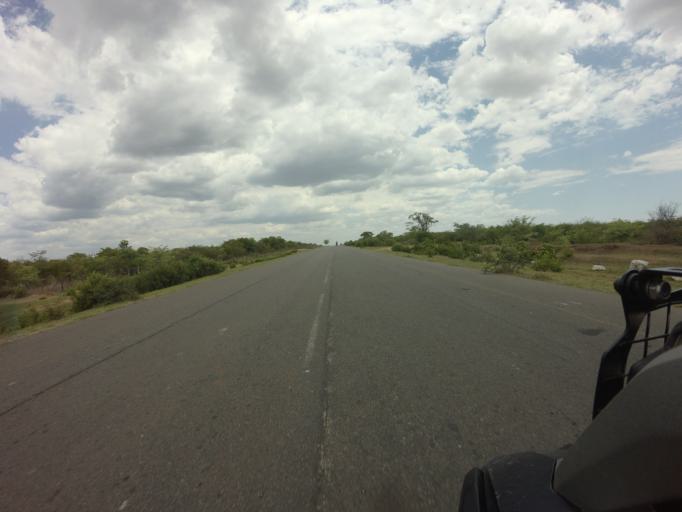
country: AO
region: Huila
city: Lubango
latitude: -15.2717
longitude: 13.8033
